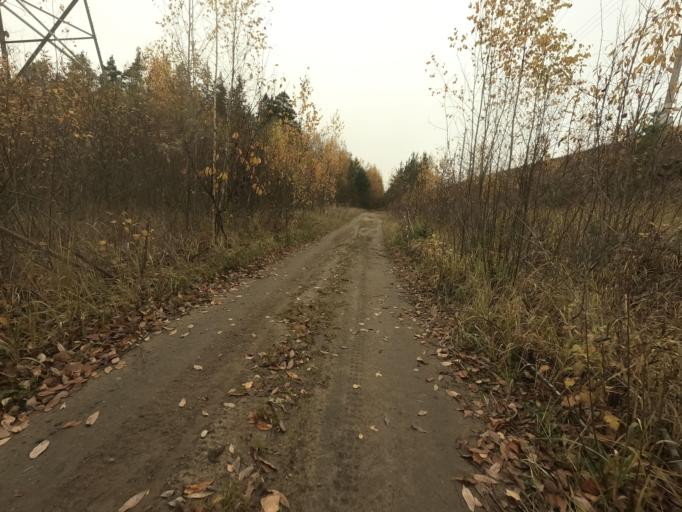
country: RU
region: Leningrad
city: Pavlovo
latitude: 59.7743
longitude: 30.9026
